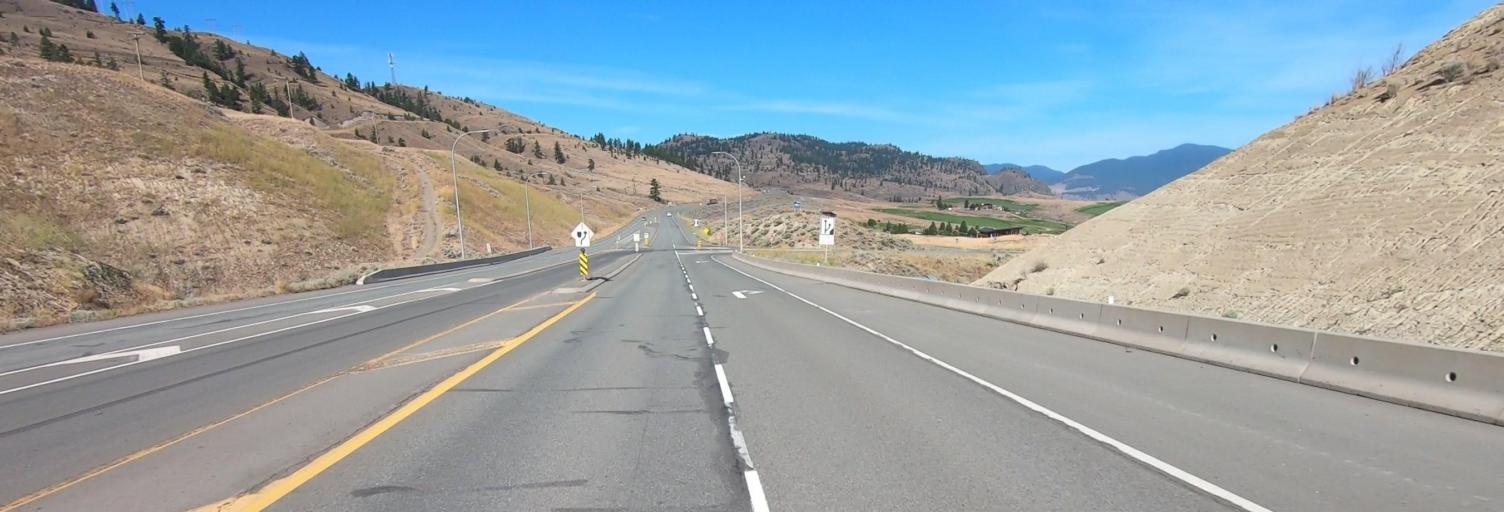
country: CA
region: British Columbia
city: Logan Lake
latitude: 50.7321
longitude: -120.6916
